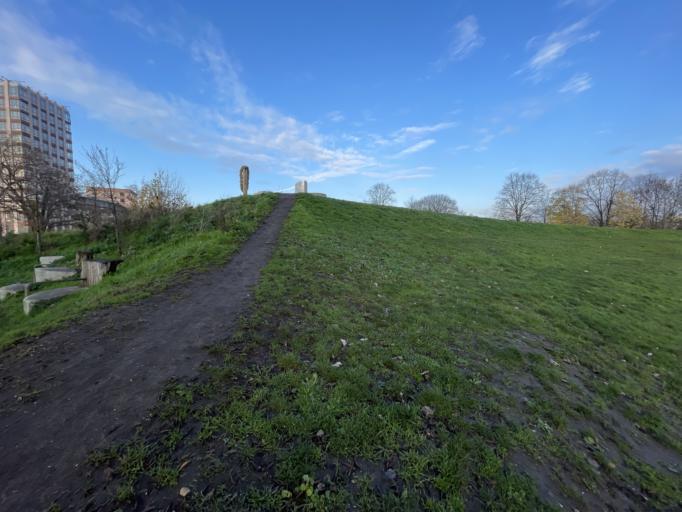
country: GB
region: England
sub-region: Greater London
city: Poplar
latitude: 51.5292
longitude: -0.0063
